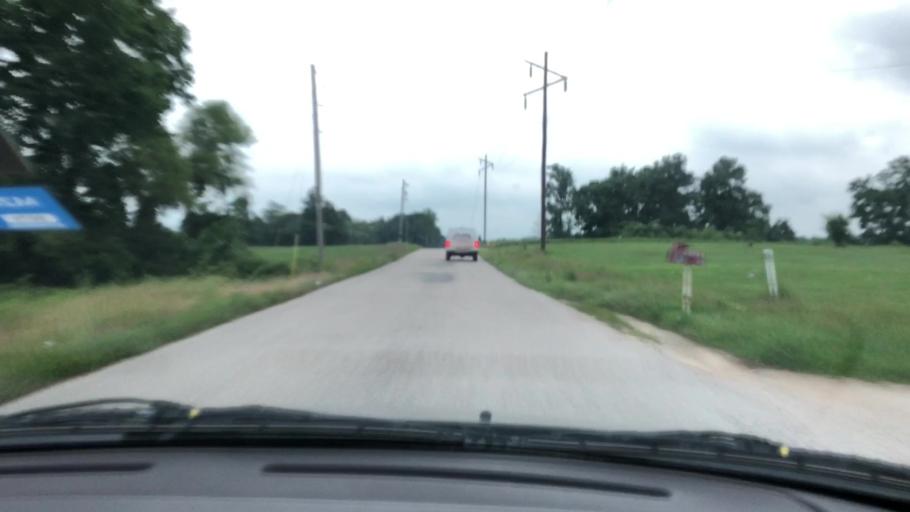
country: US
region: Indiana
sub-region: Greene County
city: Linton
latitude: 38.9826
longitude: -87.2981
